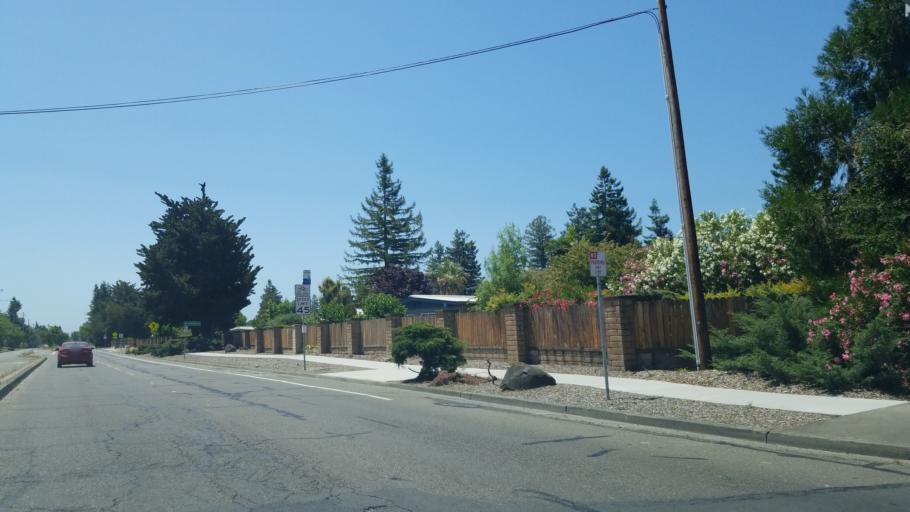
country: US
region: California
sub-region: Sonoma County
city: Roseland
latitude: 38.4453
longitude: -122.7696
